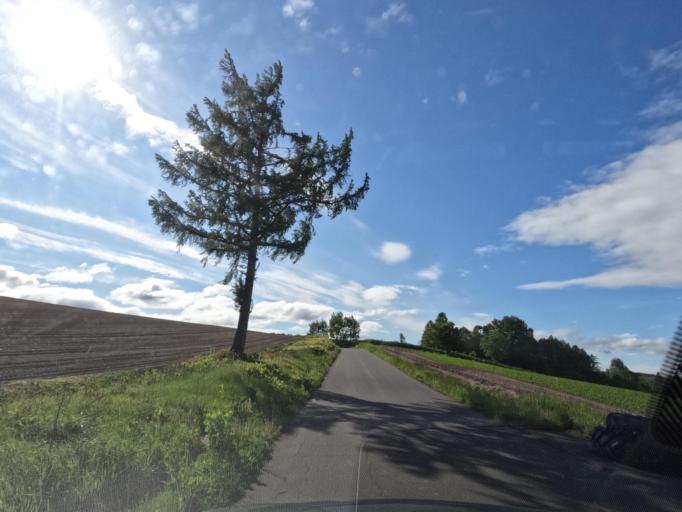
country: JP
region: Hokkaido
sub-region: Asahikawa-shi
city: Asahikawa
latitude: 43.5982
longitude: 142.4282
